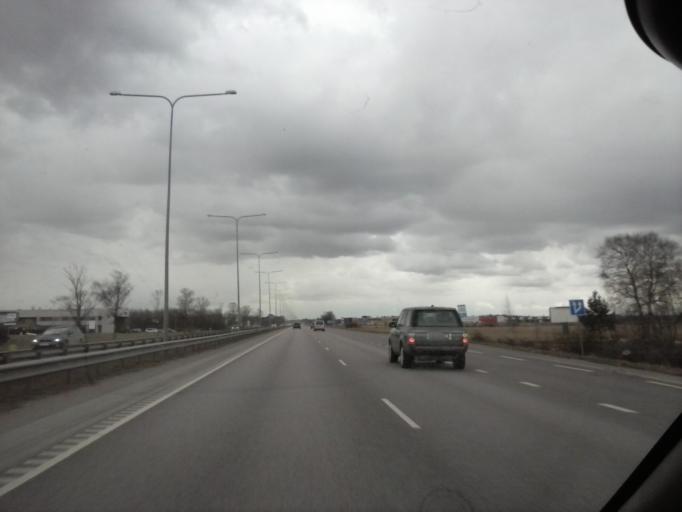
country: EE
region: Harju
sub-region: Tallinna linn
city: Tallinn
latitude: 59.3979
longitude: 24.8185
